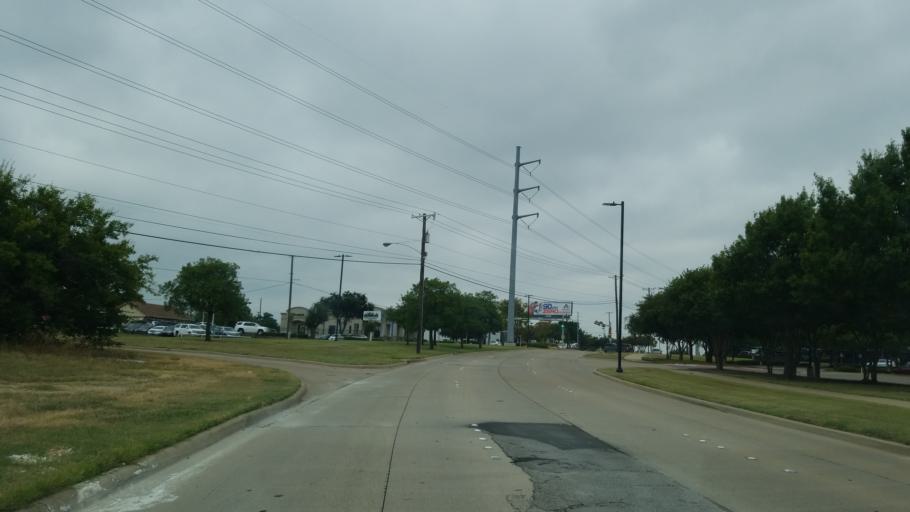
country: US
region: Texas
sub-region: Dallas County
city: Garland
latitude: 32.9094
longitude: -96.6550
